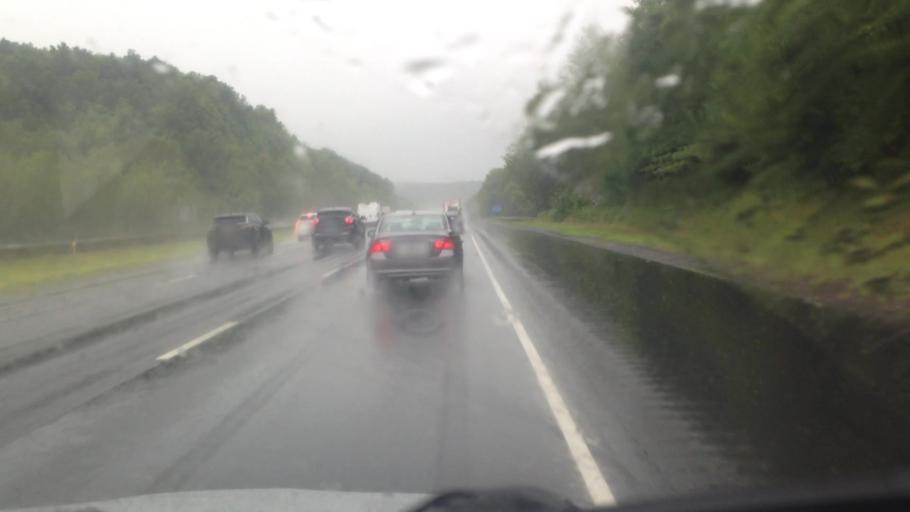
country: US
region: Connecticut
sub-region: Tolland County
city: Stafford Springs
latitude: 41.9096
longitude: -72.2707
